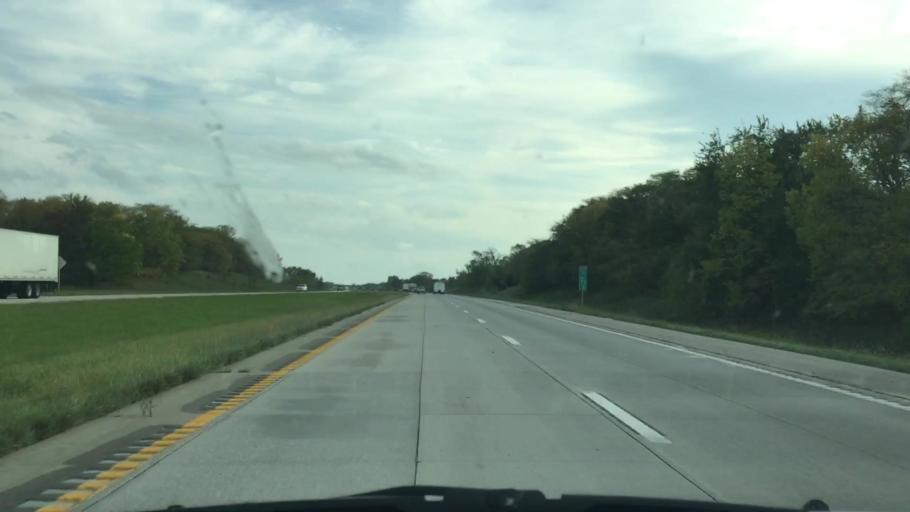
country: US
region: Missouri
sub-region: Daviess County
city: Gallatin
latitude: 40.0098
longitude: -94.0967
